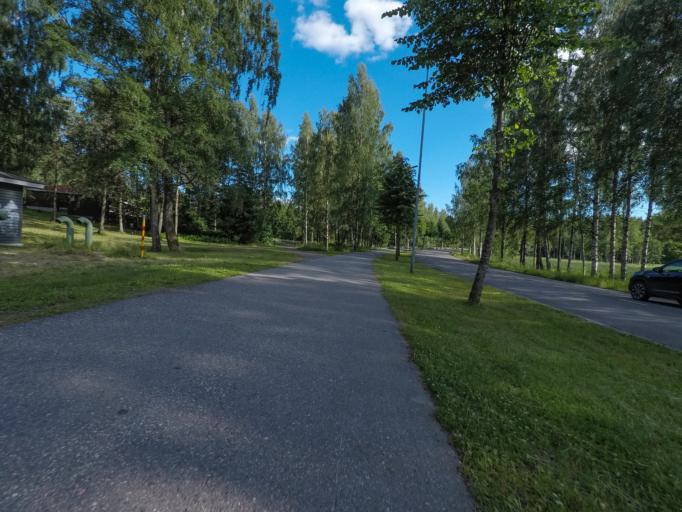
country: FI
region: South Karelia
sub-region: Lappeenranta
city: Lappeenranta
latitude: 61.0761
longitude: 28.1511
